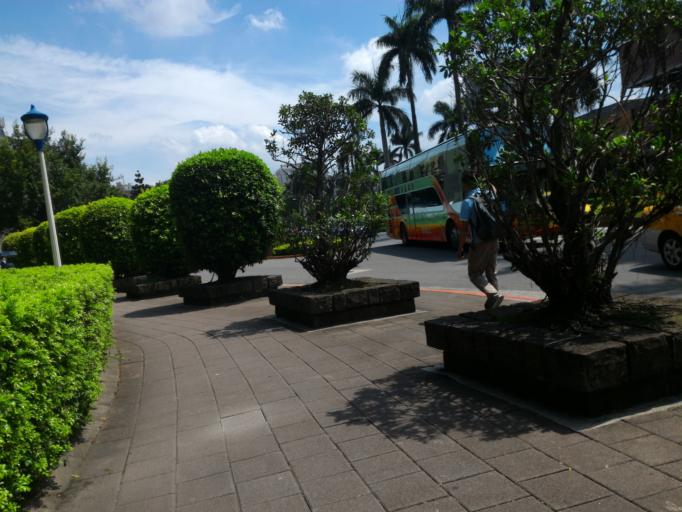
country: TW
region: Taipei
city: Taipei
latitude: 25.0377
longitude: 121.5176
